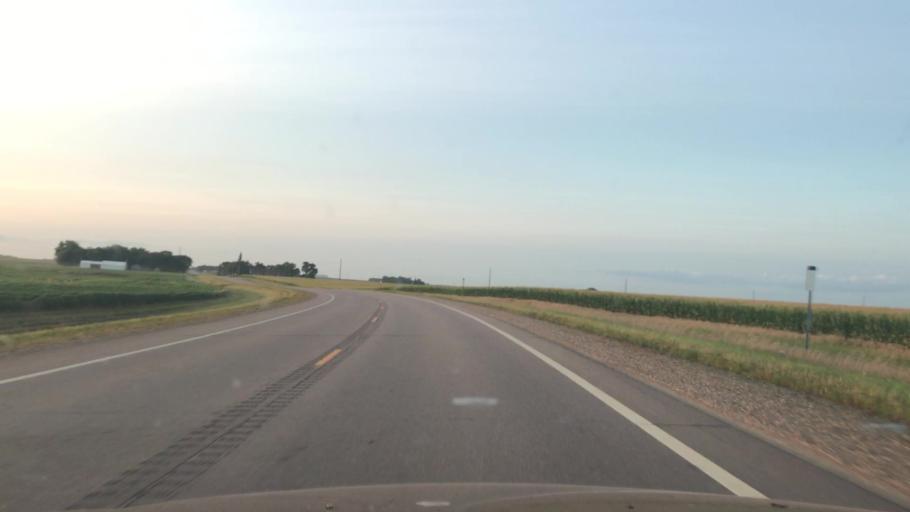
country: US
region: Minnesota
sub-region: Redwood County
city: Redwood Falls
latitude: 44.4208
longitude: -95.1178
